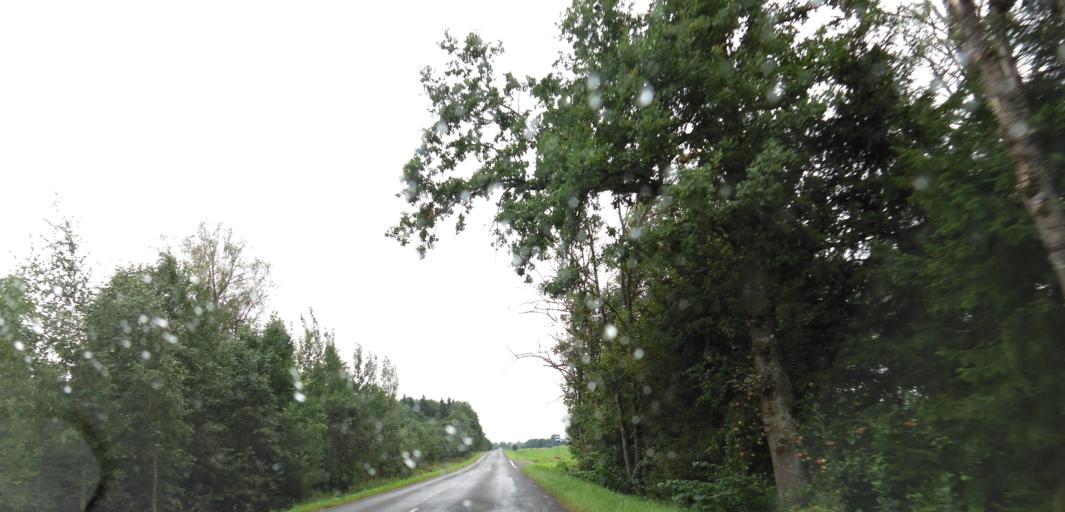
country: LT
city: Sirvintos
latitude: 55.0682
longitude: 24.9632
